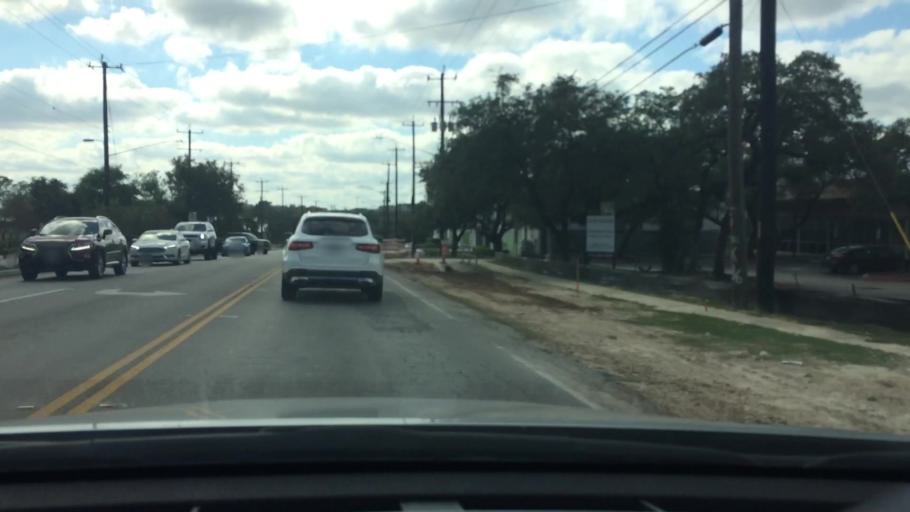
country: US
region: Texas
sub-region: Bexar County
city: Shavano Park
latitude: 29.5707
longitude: -98.5742
